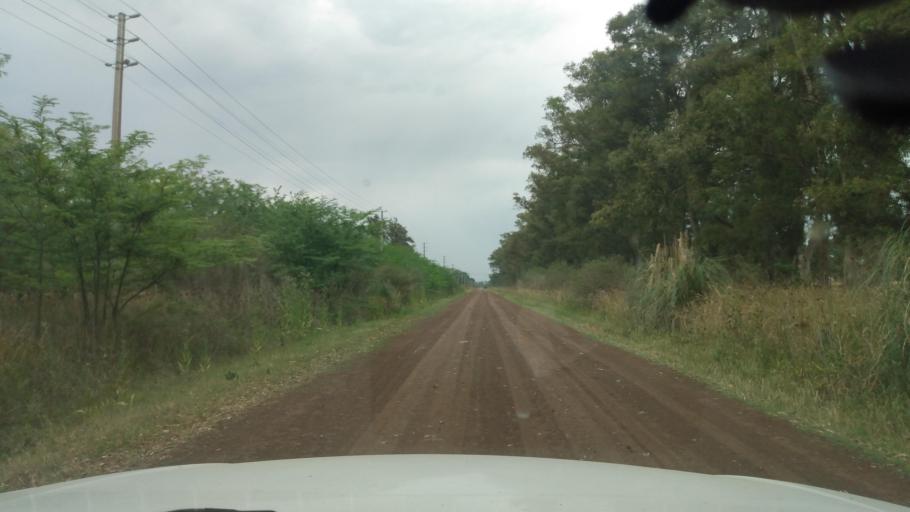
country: AR
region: Buenos Aires
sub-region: Partido de Lujan
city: Lujan
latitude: -34.5519
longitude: -59.1711
